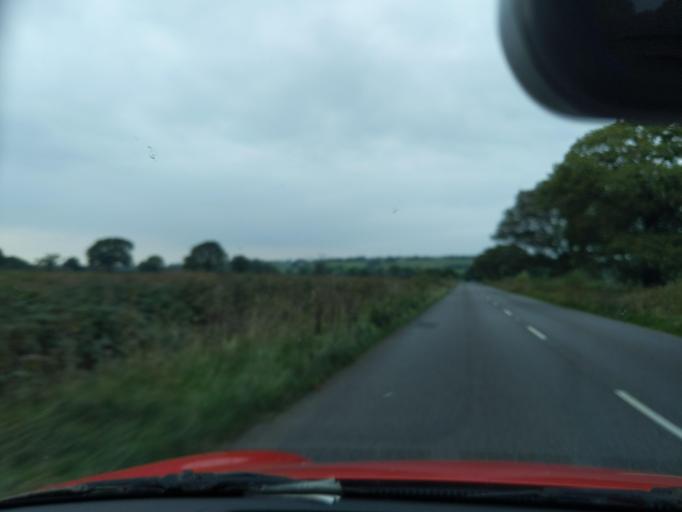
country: GB
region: England
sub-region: Devon
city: Okehampton
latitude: 50.8060
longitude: -4.0580
